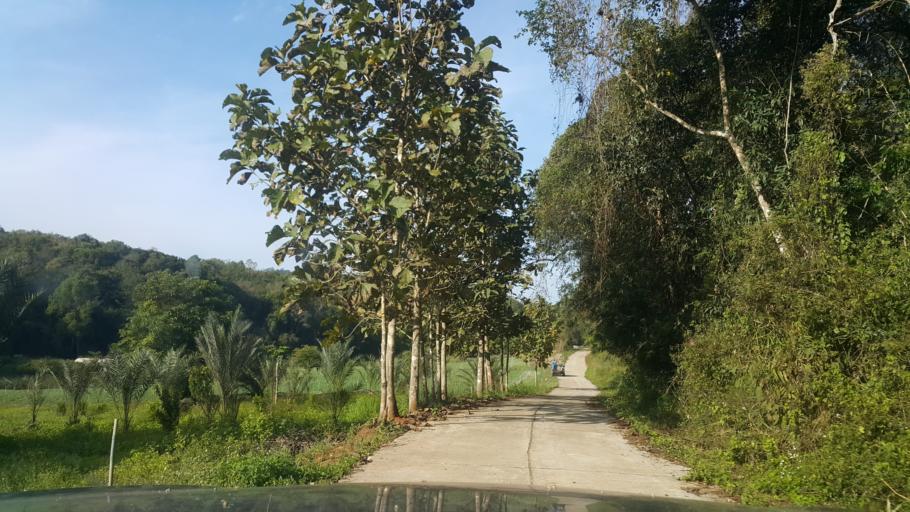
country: TH
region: Chiang Mai
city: Samoeng
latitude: 18.9956
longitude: 98.6852
